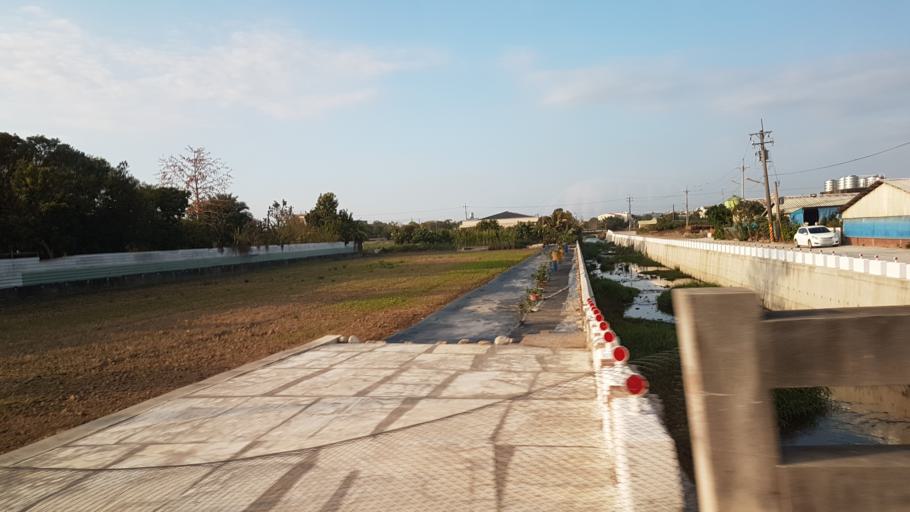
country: TW
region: Taiwan
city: Xinying
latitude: 23.3443
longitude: 120.3563
